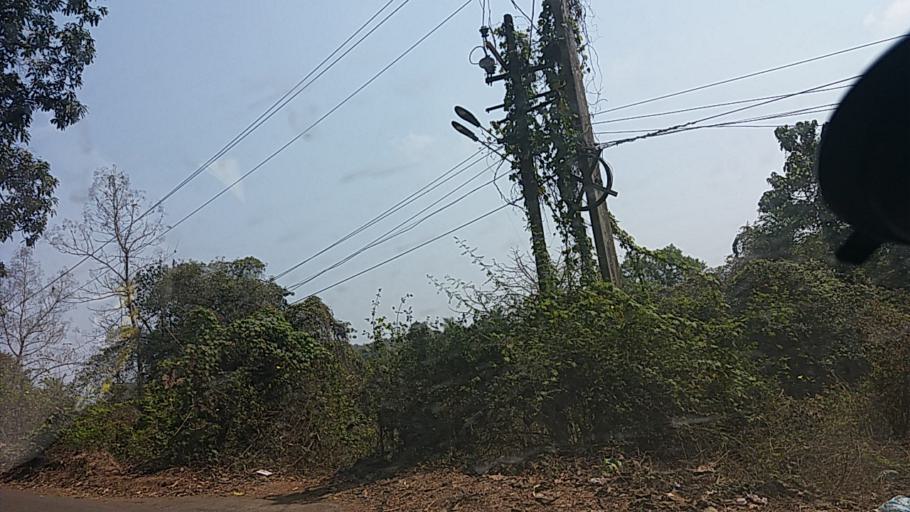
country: IN
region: Goa
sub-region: South Goa
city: Sancoale
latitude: 15.3683
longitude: 73.9160
